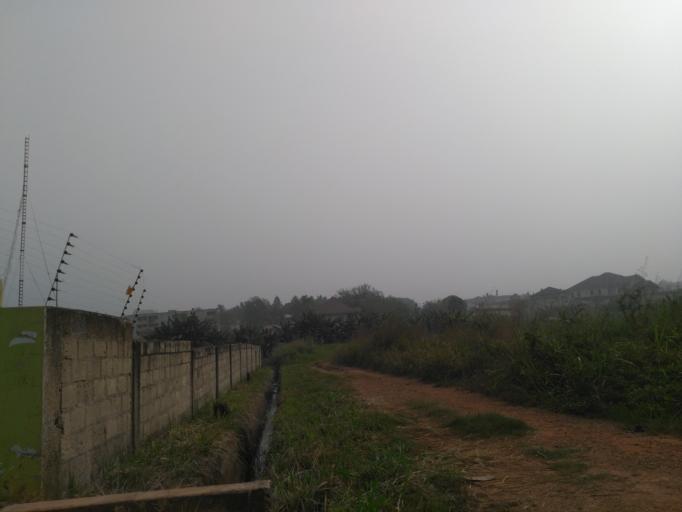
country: GH
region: Ashanti
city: Kumasi
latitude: 6.6559
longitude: -1.6258
